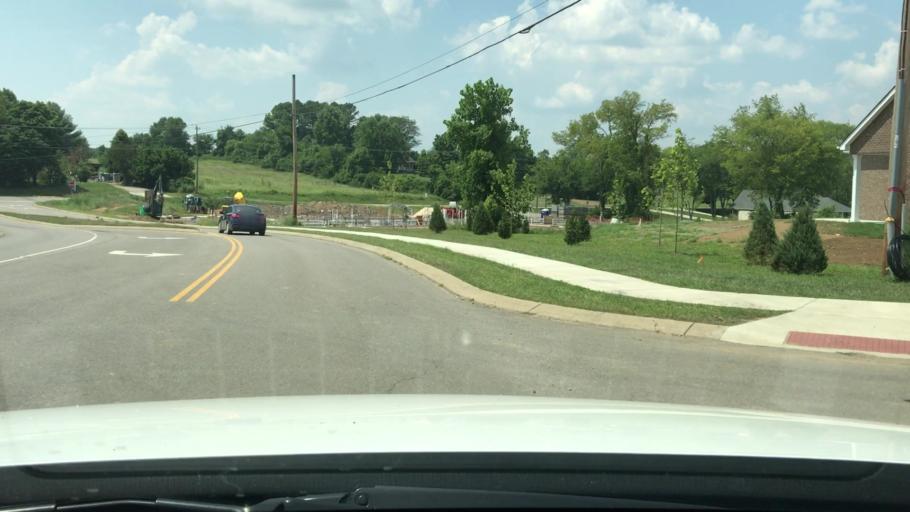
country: US
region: Tennessee
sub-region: Sumner County
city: Gallatin
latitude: 36.3606
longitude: -86.4477
